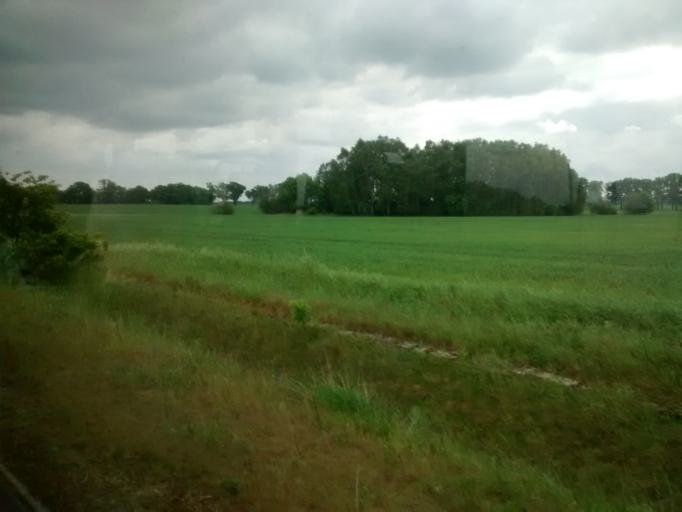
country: DE
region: Brandenburg
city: Glienicke
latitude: 52.6623
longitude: 13.3512
